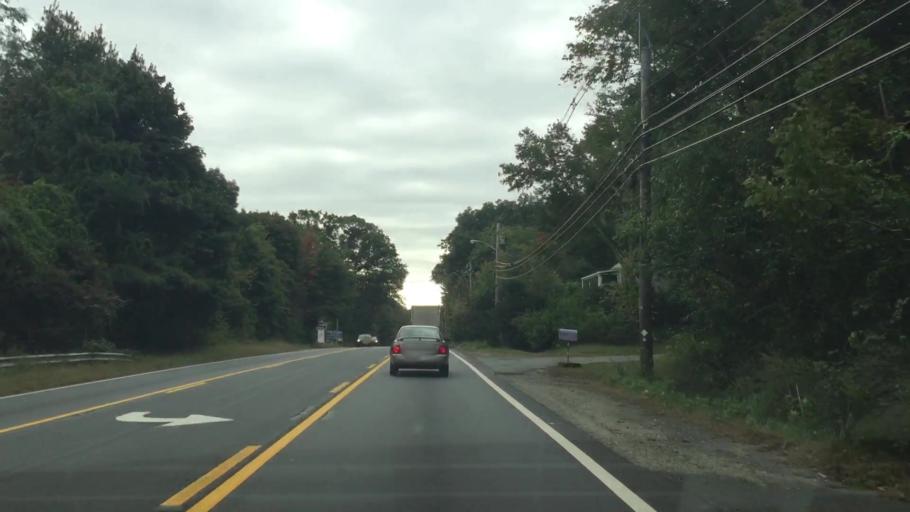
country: US
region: Massachusetts
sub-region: Essex County
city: Andover
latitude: 42.6433
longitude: -71.0857
